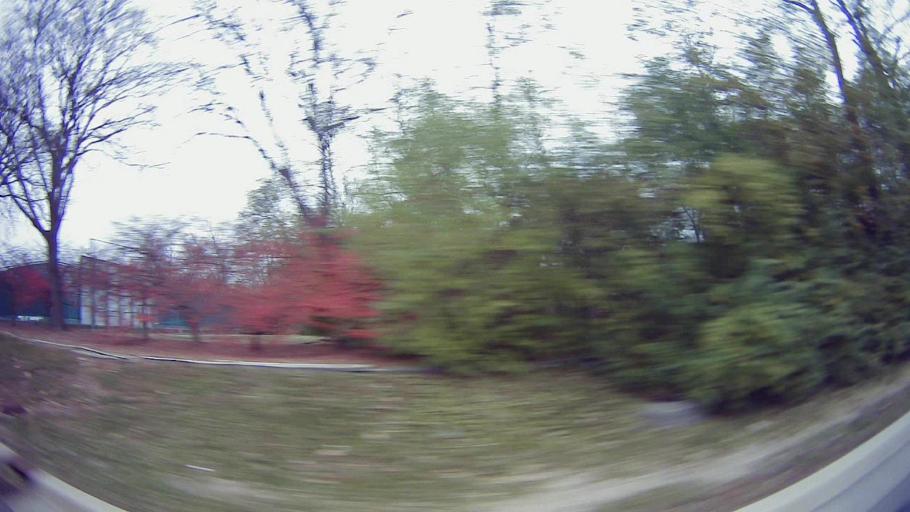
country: US
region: Michigan
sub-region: Oakland County
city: Bingham Farms
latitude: 42.5161
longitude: -83.2666
